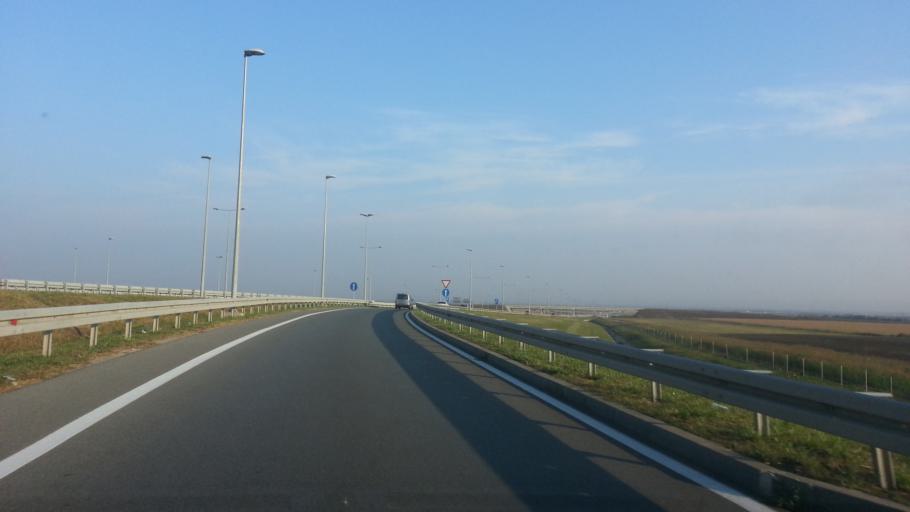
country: RS
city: Dobanovci
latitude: 44.8371
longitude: 20.2516
